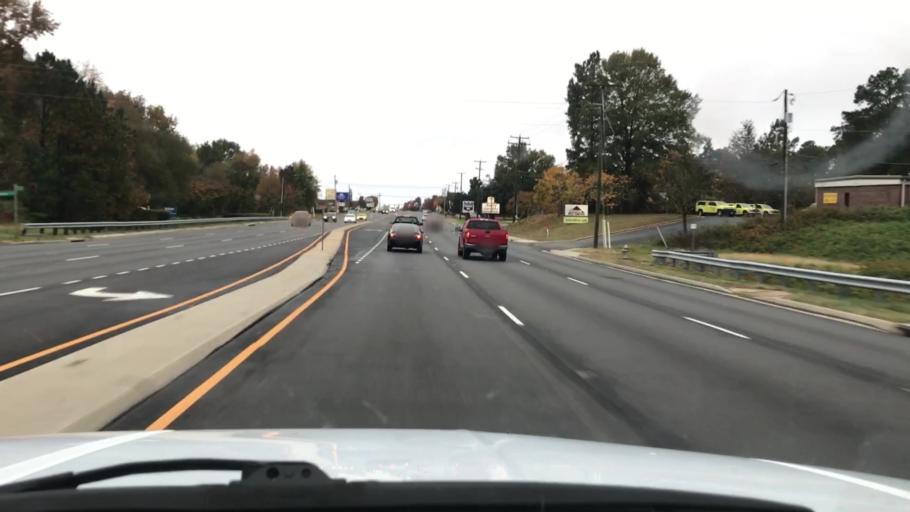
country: US
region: Virginia
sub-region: Henrico County
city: Chamberlayne
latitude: 37.6479
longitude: -77.4599
